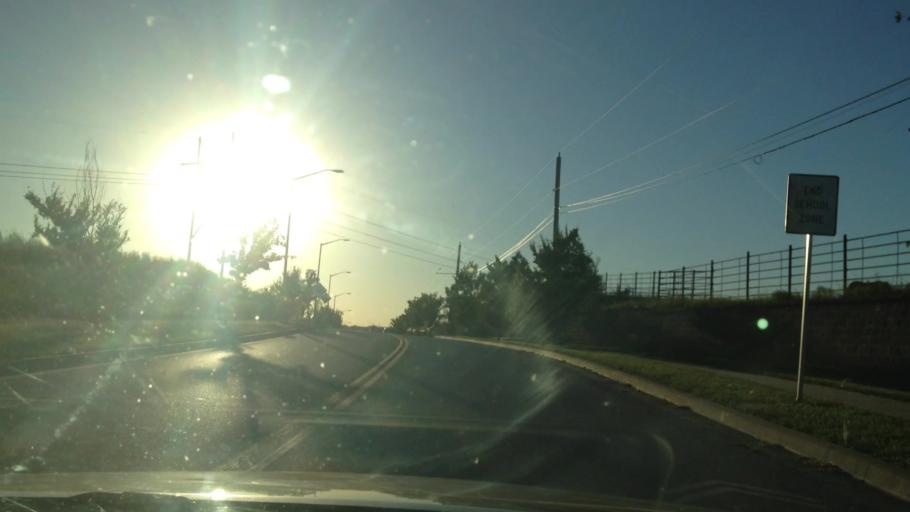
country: US
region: Missouri
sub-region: Clay County
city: Pleasant Valley
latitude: 39.2886
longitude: -94.4967
